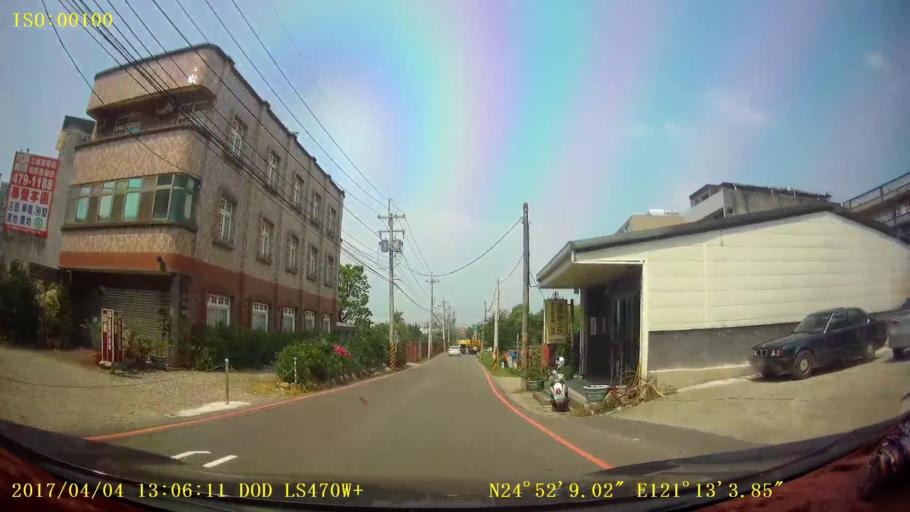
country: TW
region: Taiwan
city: Daxi
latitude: 24.8694
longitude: 121.2178
